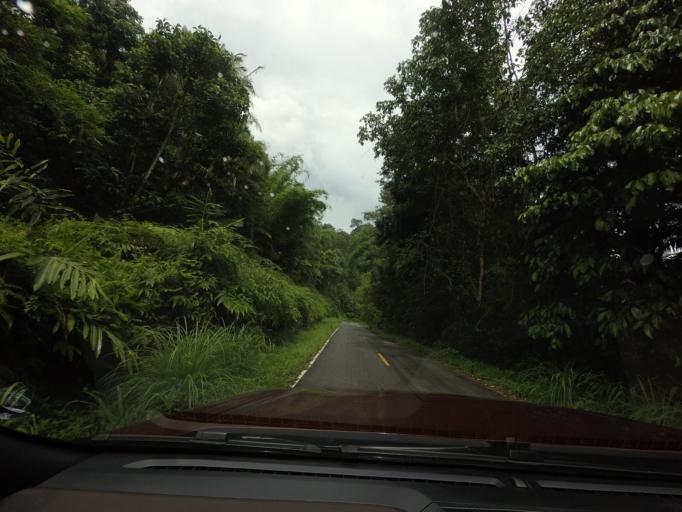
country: TH
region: Narathiwat
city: Sukhirin
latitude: 5.9445
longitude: 101.6518
